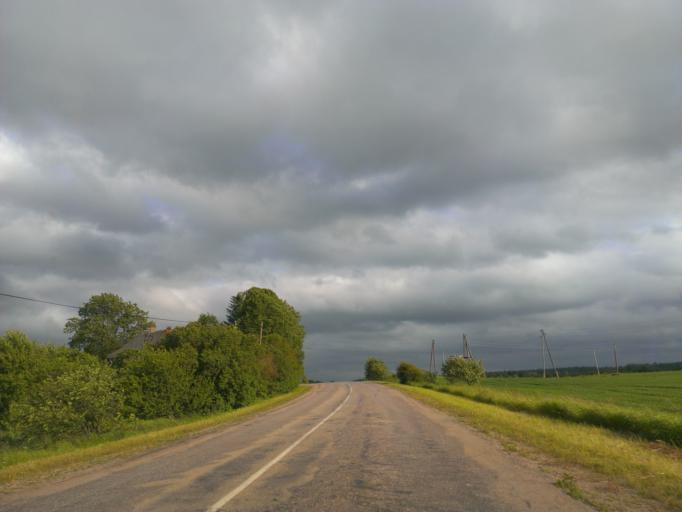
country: LV
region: Aizpute
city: Aizpute
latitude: 56.7164
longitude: 21.7602
